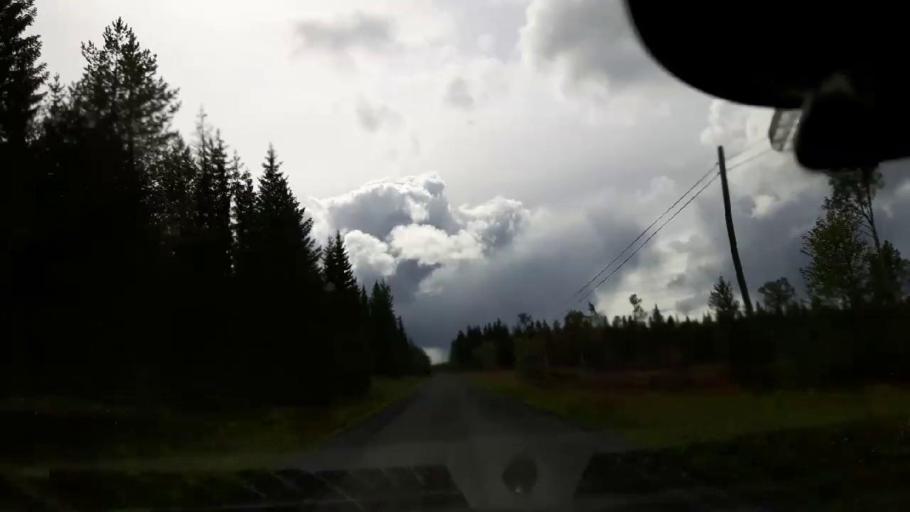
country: SE
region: Jaemtland
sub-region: Krokoms Kommun
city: Valla
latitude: 63.3627
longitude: 13.8641
